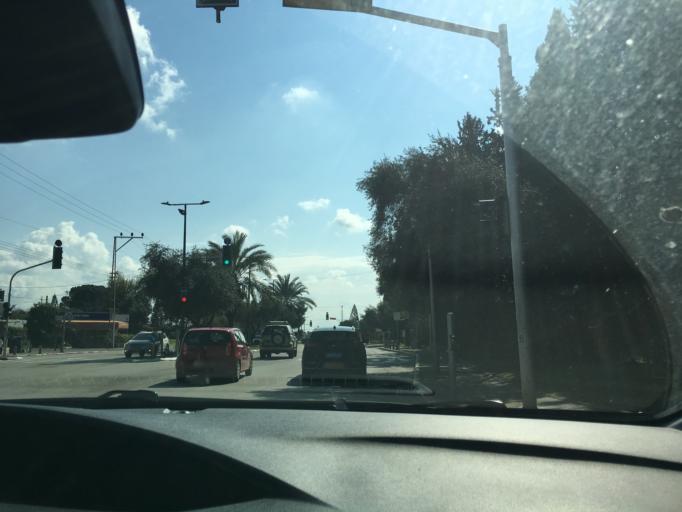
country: IL
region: Central District
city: Ra'anana
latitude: 32.1692
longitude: 34.8527
